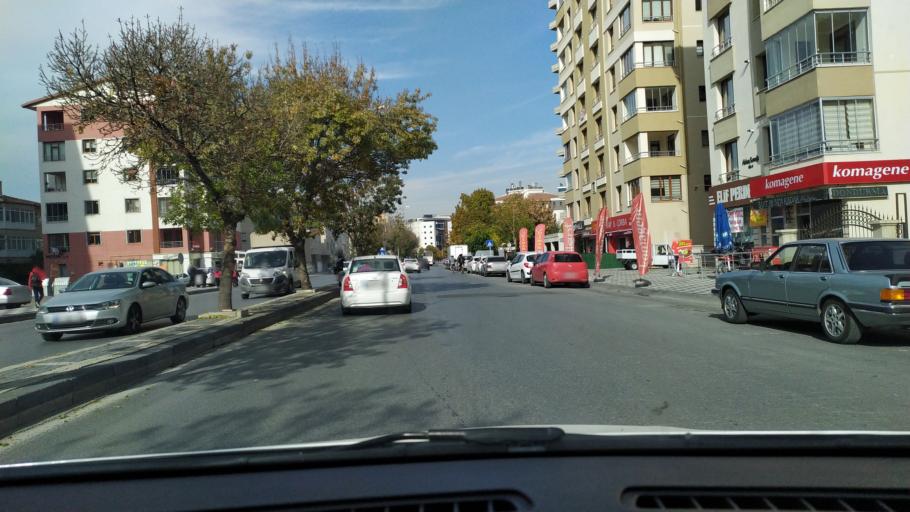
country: TR
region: Kayseri
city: Kayseri
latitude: 38.7088
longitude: 35.4917
